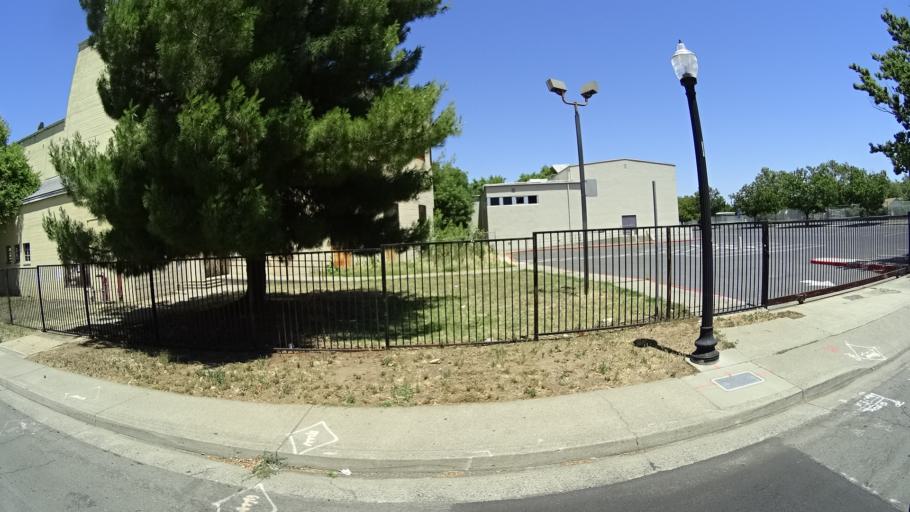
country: US
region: California
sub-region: Sacramento County
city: Sacramento
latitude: 38.5545
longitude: -121.4662
